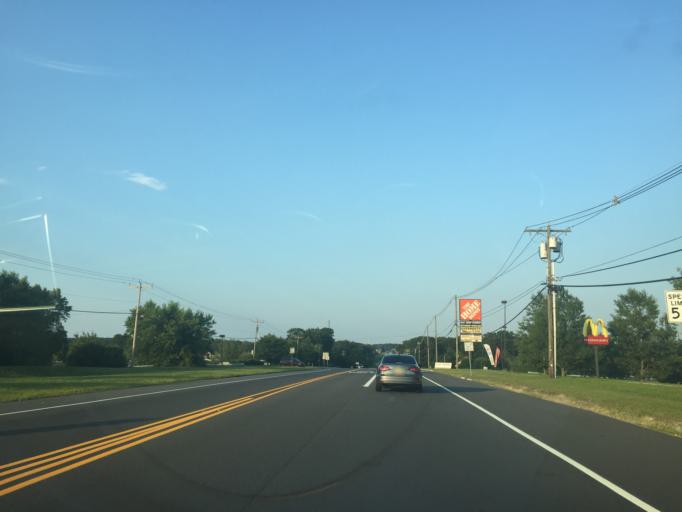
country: US
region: New Jersey
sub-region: Monmouth County
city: Shark River Hills
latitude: 40.2231
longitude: -74.0852
